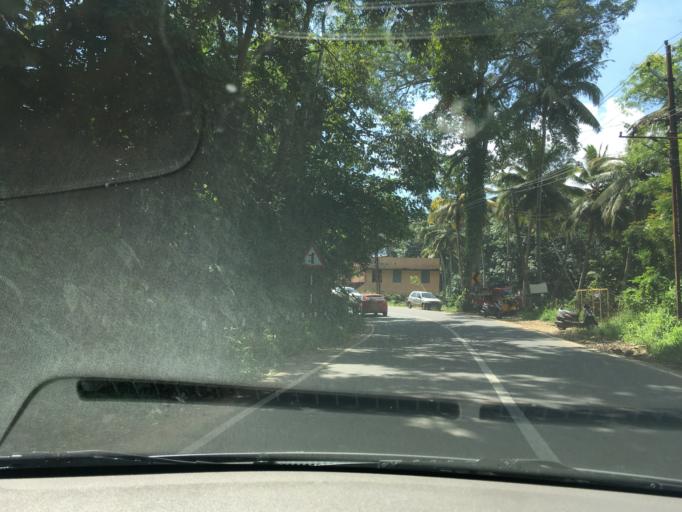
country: IN
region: Kerala
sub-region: Thiruvananthapuram
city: Nedumangad
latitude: 8.6060
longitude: 76.9989
